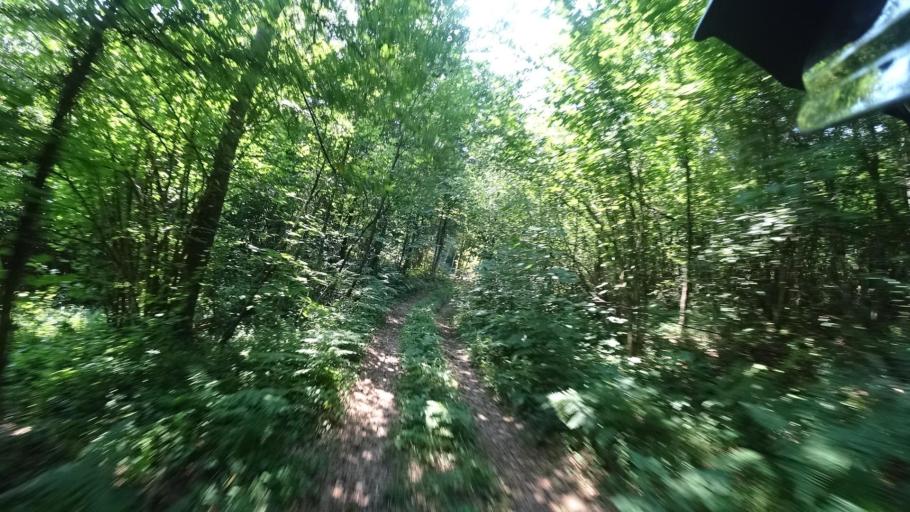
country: HR
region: Karlovacka
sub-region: Grad Ogulin
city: Ogulin
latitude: 45.3116
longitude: 15.1703
